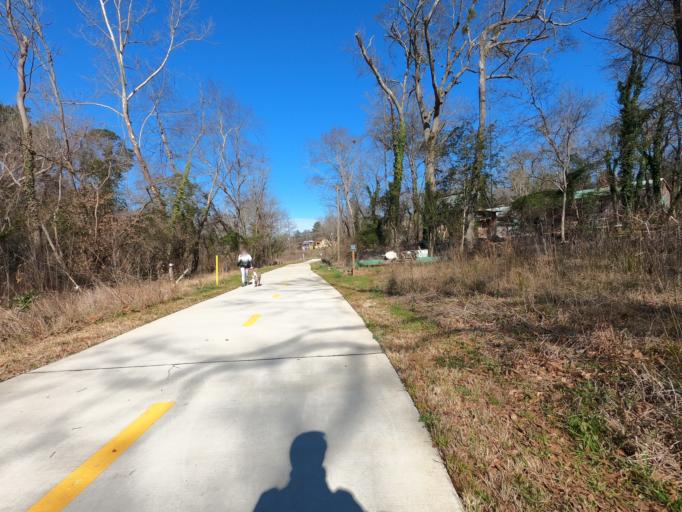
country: US
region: Georgia
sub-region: Clarke County
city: Athens
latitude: 33.9687
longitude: -83.3754
